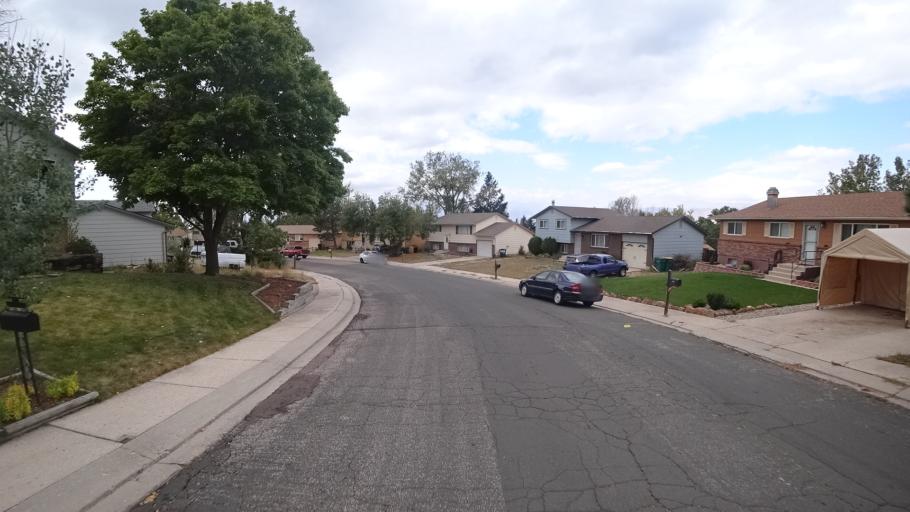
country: US
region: Colorado
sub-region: El Paso County
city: Cimarron Hills
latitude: 38.8923
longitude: -104.7354
